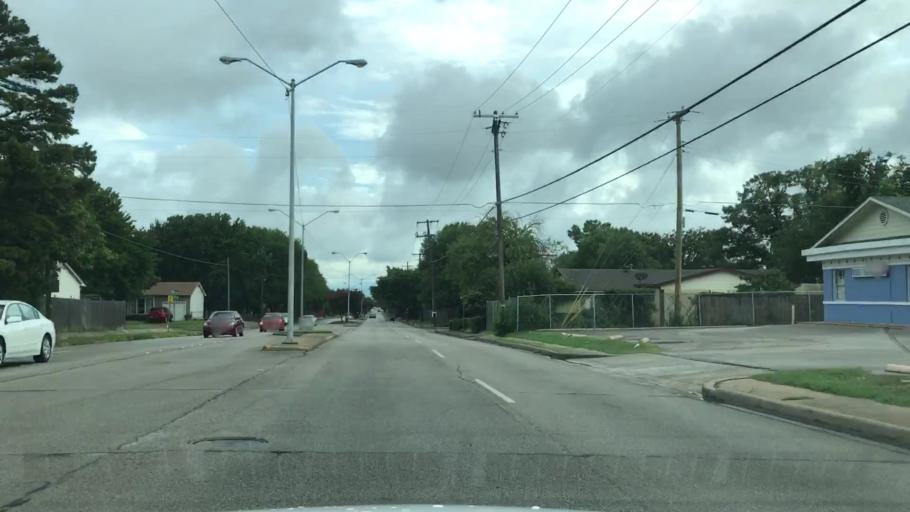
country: US
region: Texas
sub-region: Dallas County
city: Irving
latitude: 32.8502
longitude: -96.9765
